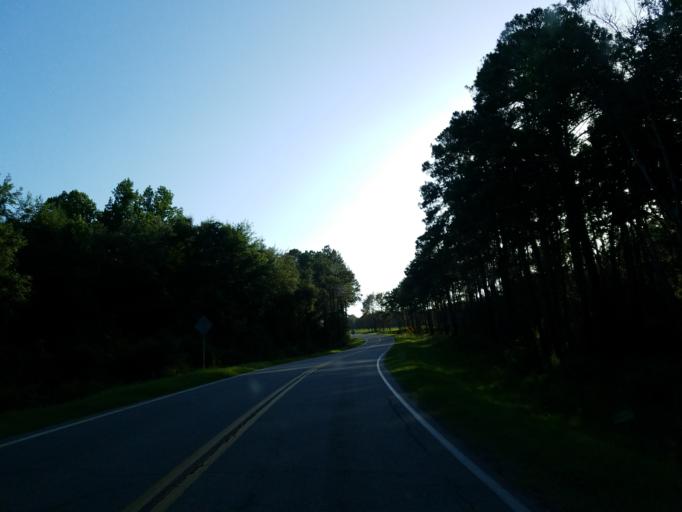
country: US
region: Georgia
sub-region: Tift County
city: Tifton
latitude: 31.6087
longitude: -83.4466
